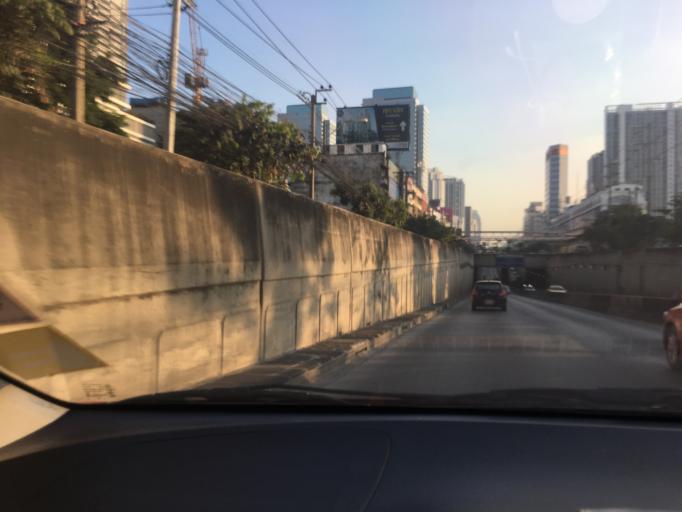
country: TH
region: Bangkok
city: Huai Khwang
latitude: 13.7914
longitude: 100.5743
